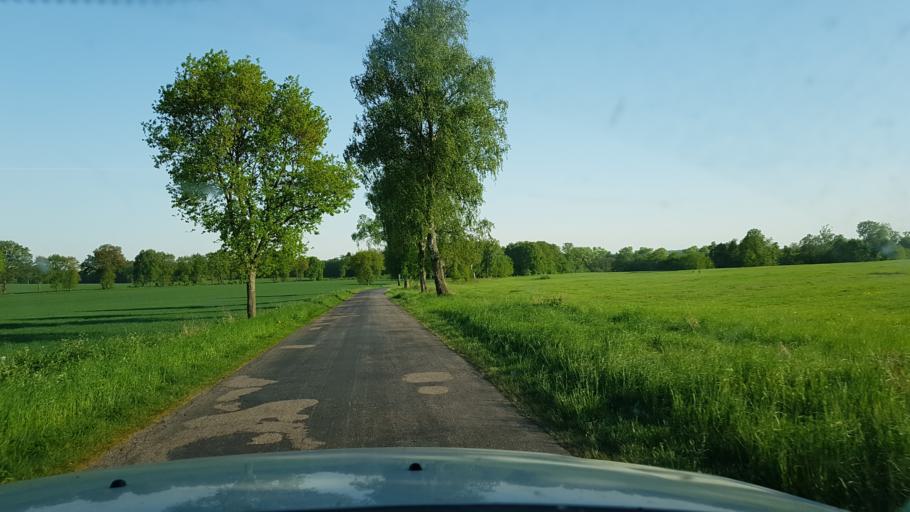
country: PL
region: West Pomeranian Voivodeship
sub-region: Powiat lobeski
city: Dobra
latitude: 53.6012
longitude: 15.3322
